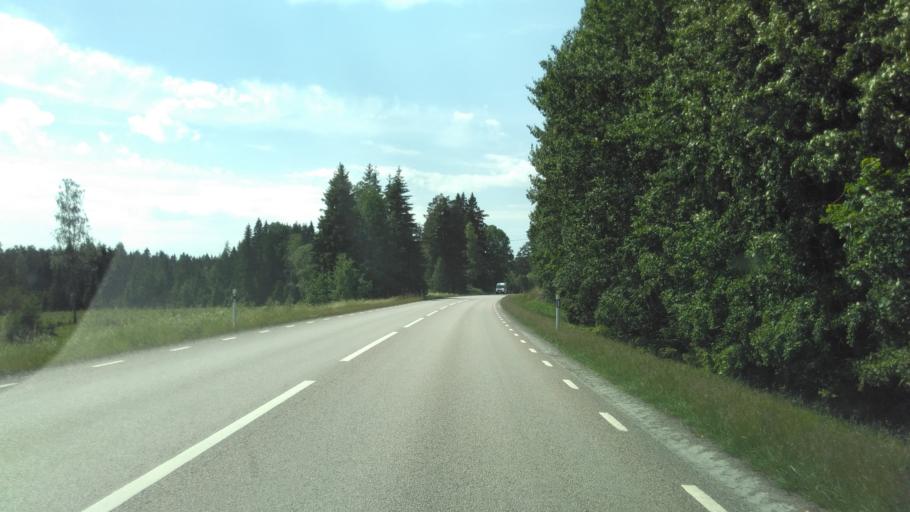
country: SE
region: Vaestra Goetaland
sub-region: Vara Kommun
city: Vara
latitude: 58.4354
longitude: 12.9166
